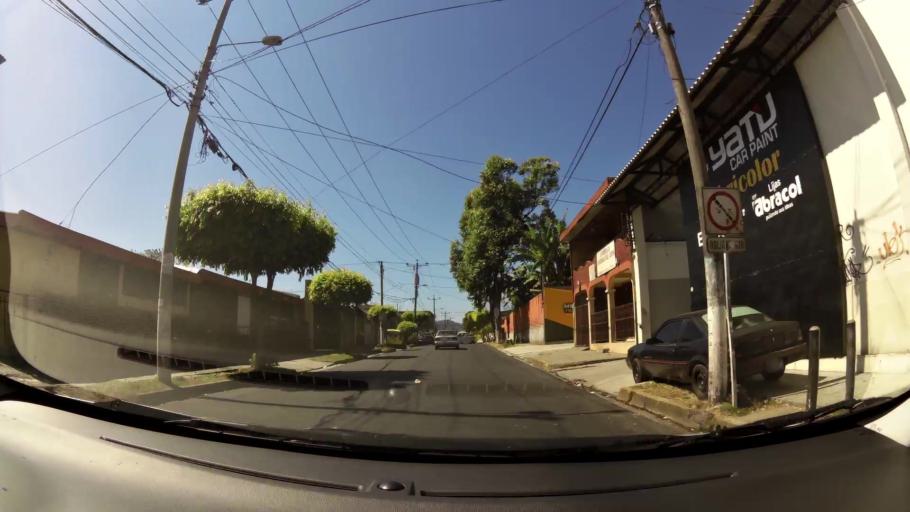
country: SV
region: La Libertad
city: Santa Tecla
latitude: 13.6764
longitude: -89.2849
